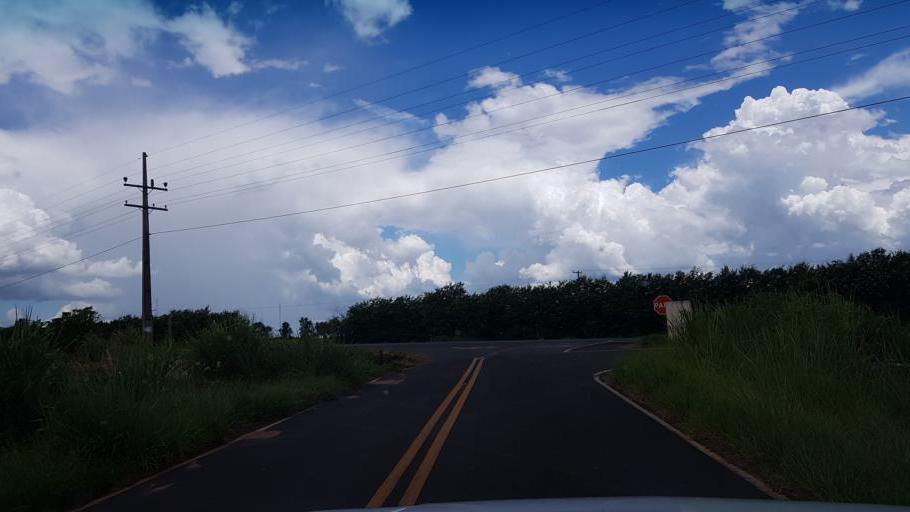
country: BR
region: Sao Paulo
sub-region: Paraguacu Paulista
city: Paraguacu Paulista
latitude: -22.3650
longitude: -50.6292
